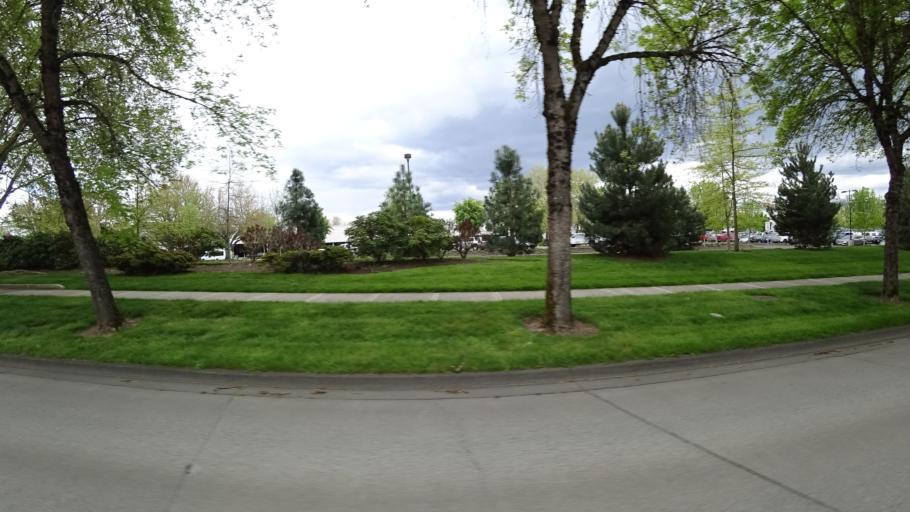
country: US
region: Oregon
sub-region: Washington County
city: Rockcreek
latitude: 45.5464
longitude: -122.9261
